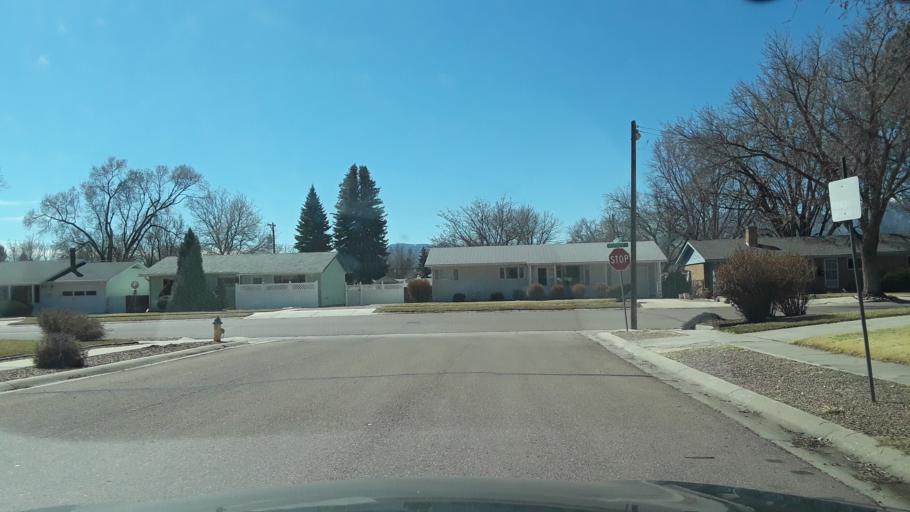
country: US
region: Colorado
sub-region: El Paso County
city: Colorado Springs
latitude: 38.8710
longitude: -104.8068
